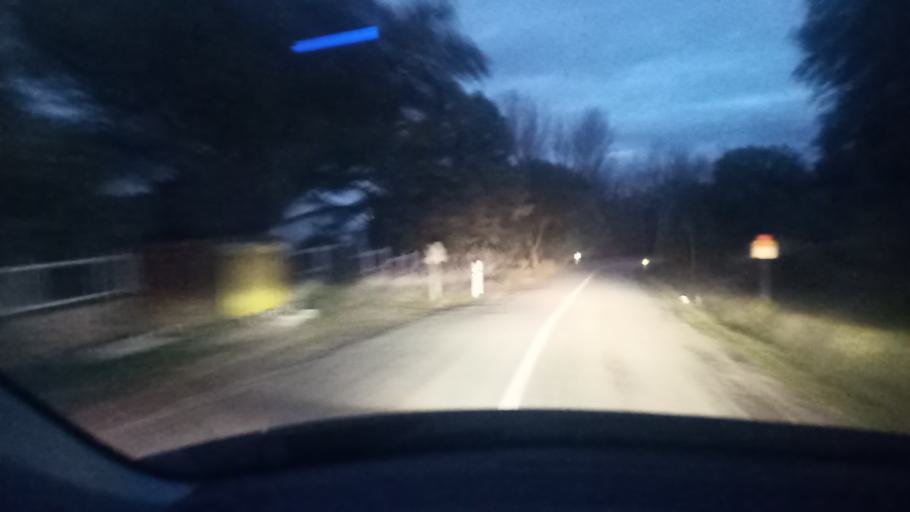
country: ES
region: Madrid
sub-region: Provincia de Madrid
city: Colmenar del Arroyo
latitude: 40.4269
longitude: -4.2055
